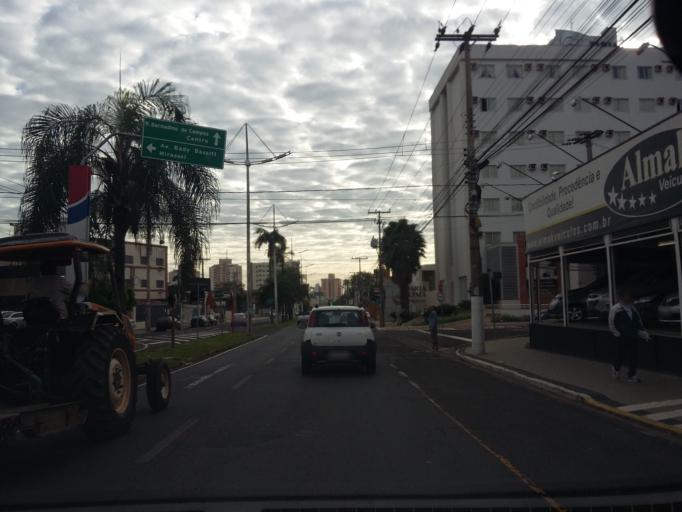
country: BR
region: Sao Paulo
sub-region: Sao Jose Do Rio Preto
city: Sao Jose do Rio Preto
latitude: -20.8254
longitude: -49.3943
